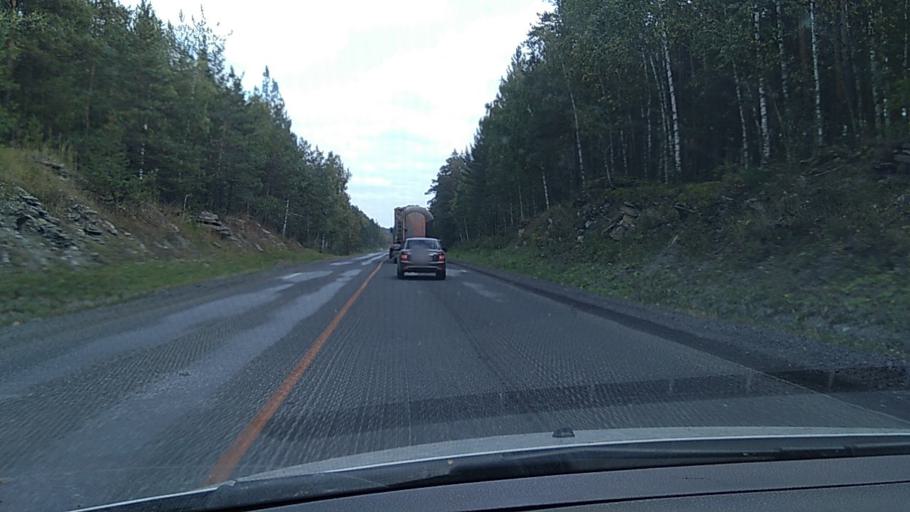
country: RU
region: Chelyabinsk
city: Miass
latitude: 54.9301
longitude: 60.1819
